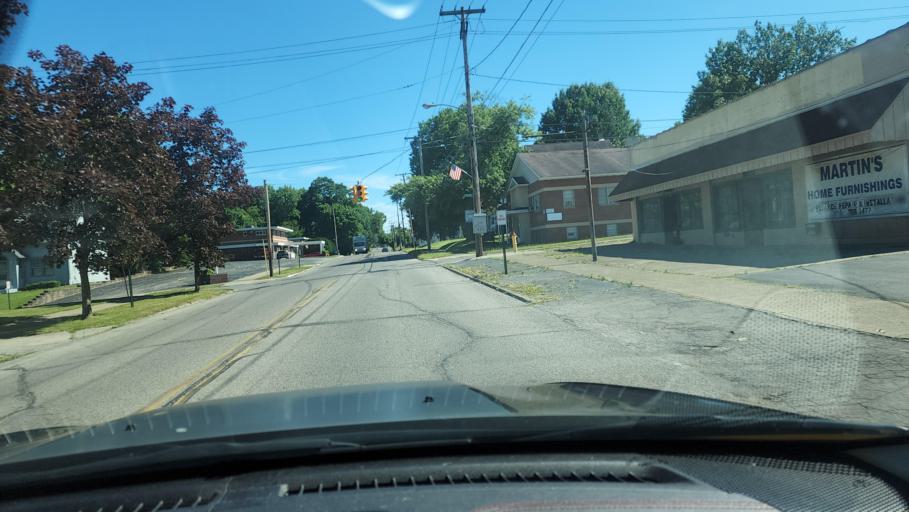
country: US
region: Ohio
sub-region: Mahoning County
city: Struthers
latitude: 41.0540
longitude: -80.6036
